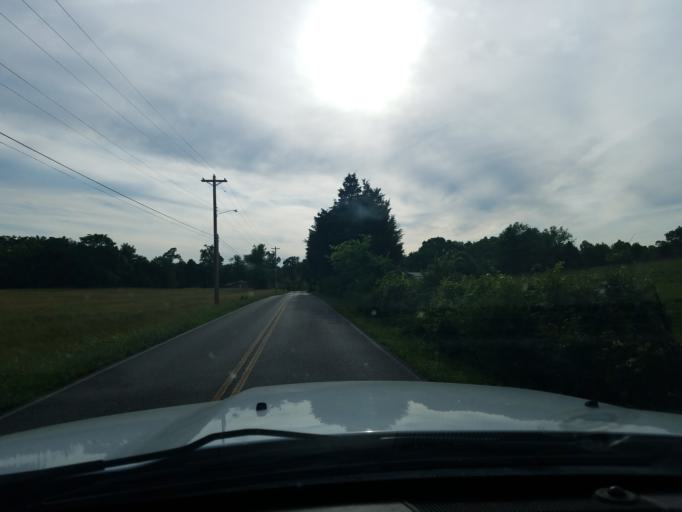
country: US
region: Tennessee
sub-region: Putnam County
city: Cookeville
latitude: 36.1285
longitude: -85.5548
